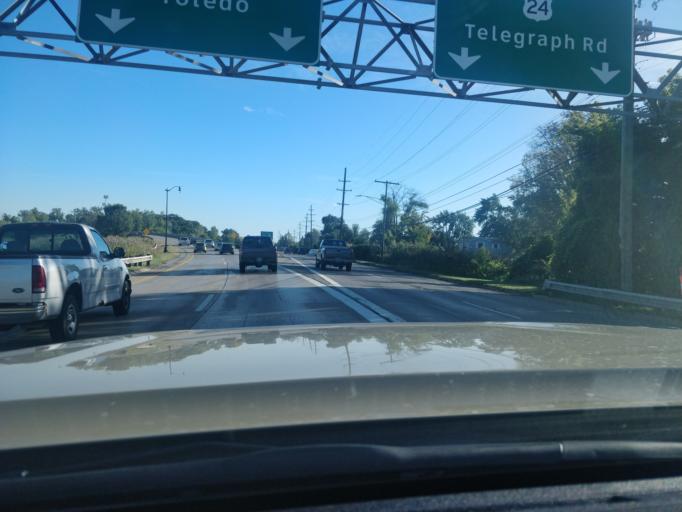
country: US
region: Michigan
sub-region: Wayne County
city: Taylor
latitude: 42.1951
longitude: -83.2680
